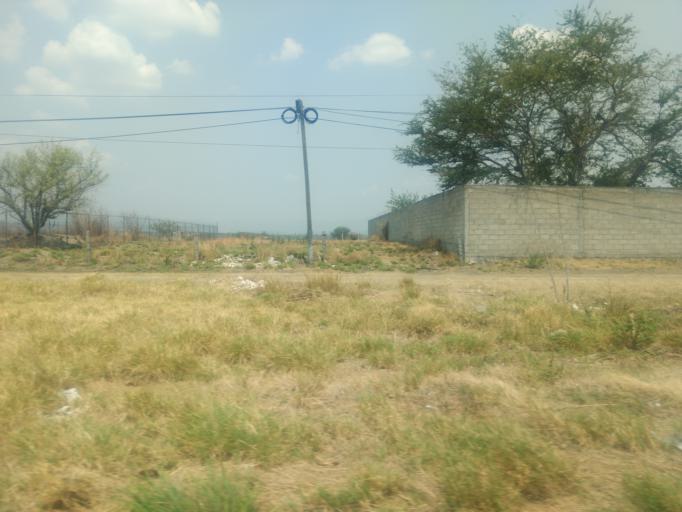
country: MX
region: Morelos
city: Ahuehuetzingo
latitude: 18.6891
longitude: -99.2849
